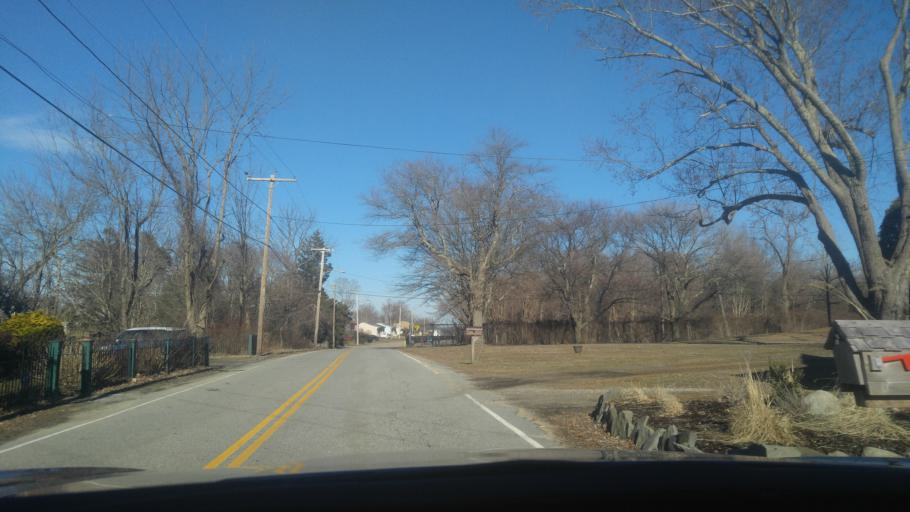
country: US
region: Rhode Island
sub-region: Kent County
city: East Greenwich
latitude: 41.6331
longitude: -71.4134
